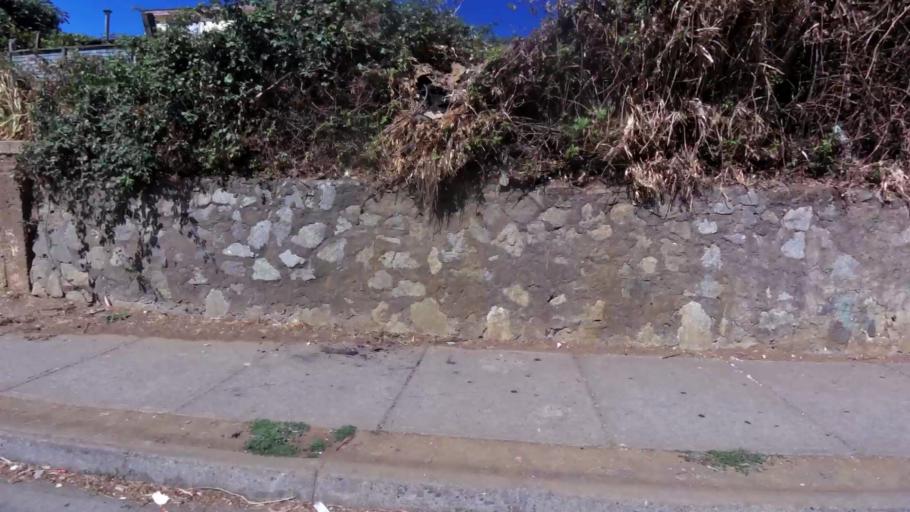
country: CL
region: Biobio
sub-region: Provincia de Concepcion
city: Penco
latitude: -36.7265
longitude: -72.9866
